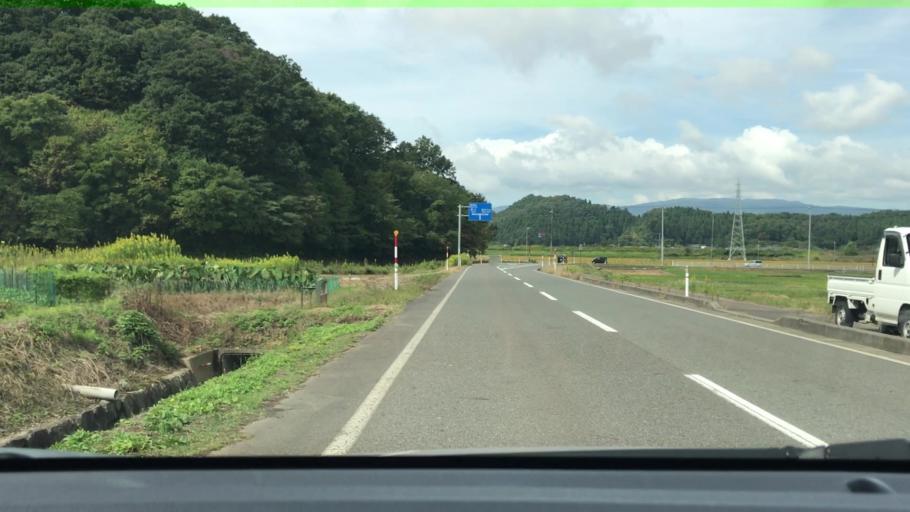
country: JP
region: Fukui
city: Fukui-shi
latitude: 36.0226
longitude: 136.1810
